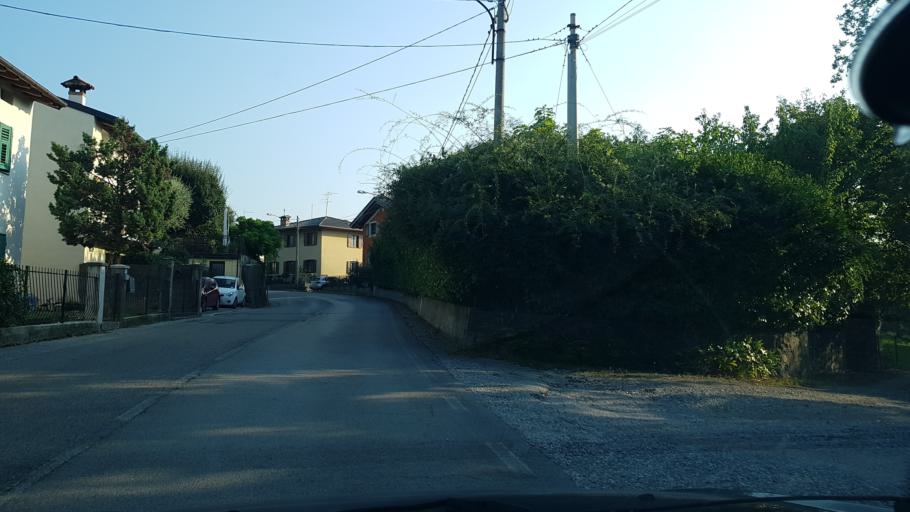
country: IT
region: Friuli Venezia Giulia
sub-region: Provincia di Gorizia
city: San Floriano del Collio
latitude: 45.9725
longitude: 13.6123
